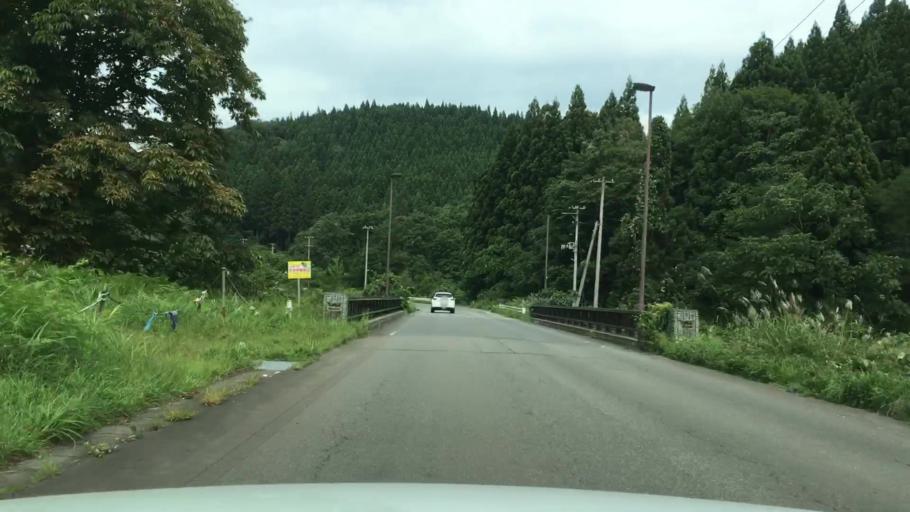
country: JP
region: Aomori
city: Shimokizukuri
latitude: 40.7453
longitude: 140.2409
